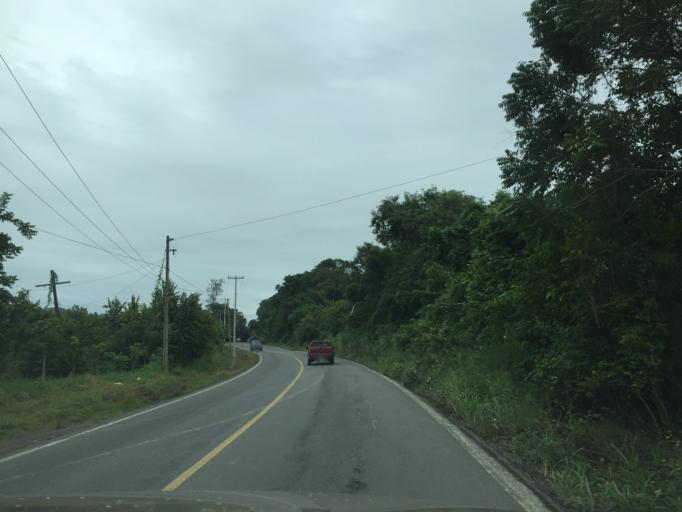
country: MX
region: Veracruz
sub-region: Papantla
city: El Chote
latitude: 20.4382
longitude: -97.3912
